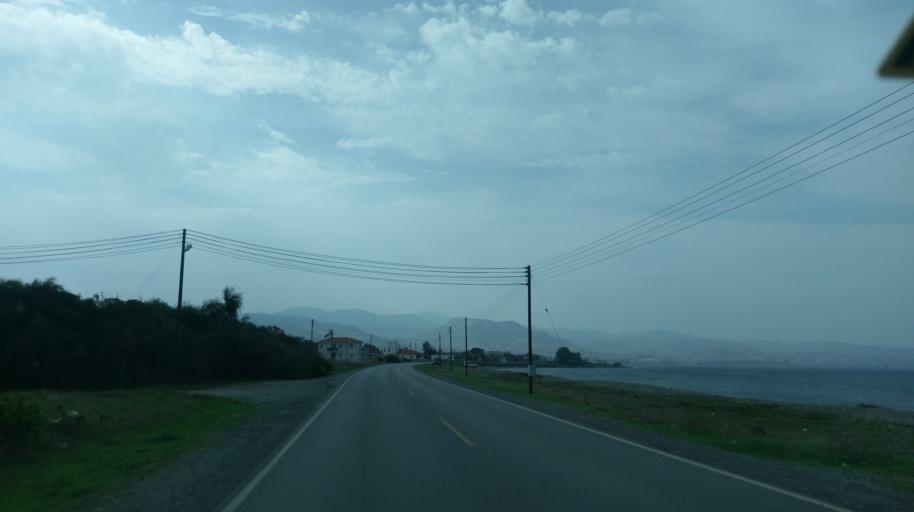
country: CY
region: Lefkosia
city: Lefka
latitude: 35.1496
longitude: 32.8555
